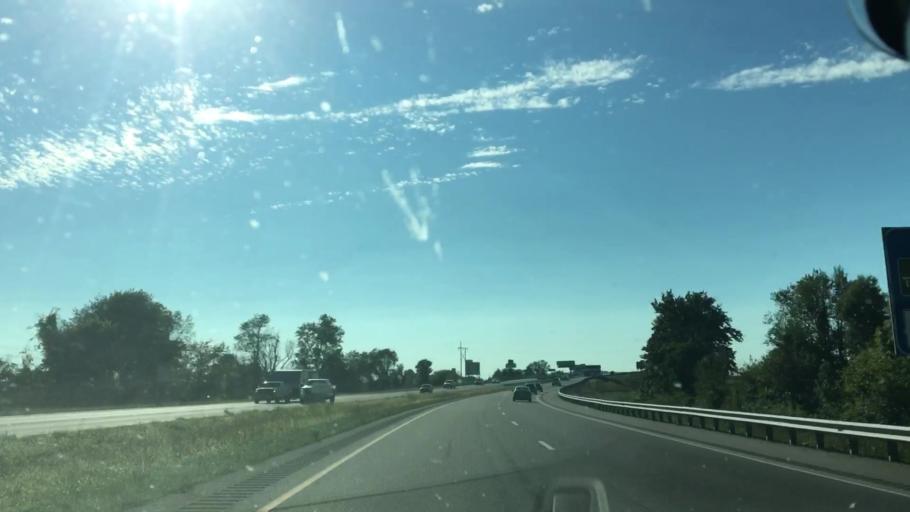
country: US
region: Kentucky
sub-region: Daviess County
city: Owensboro
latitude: 37.7253
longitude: -87.1039
